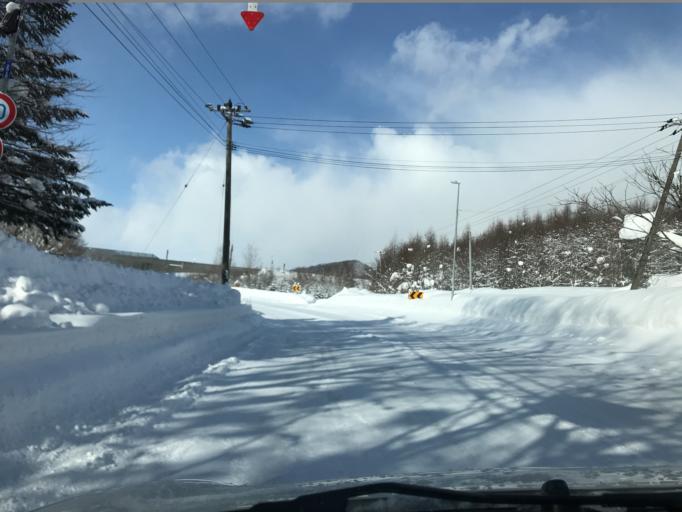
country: JP
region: Hokkaido
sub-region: Asahikawa-shi
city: Asahikawa
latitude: 43.9323
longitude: 142.4718
